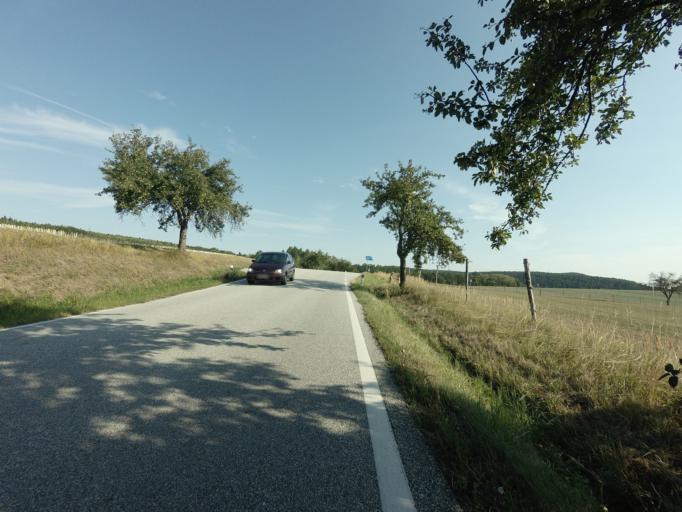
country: CZ
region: Jihocesky
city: Tyn nad Vltavou
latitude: 49.2604
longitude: 14.4133
